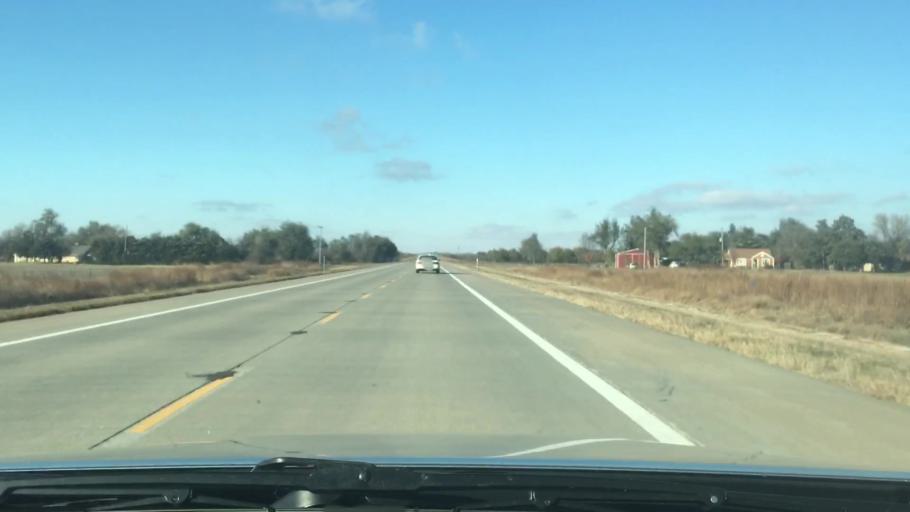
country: US
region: Kansas
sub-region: Reno County
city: Hutchinson
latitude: 38.0697
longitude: -97.9869
